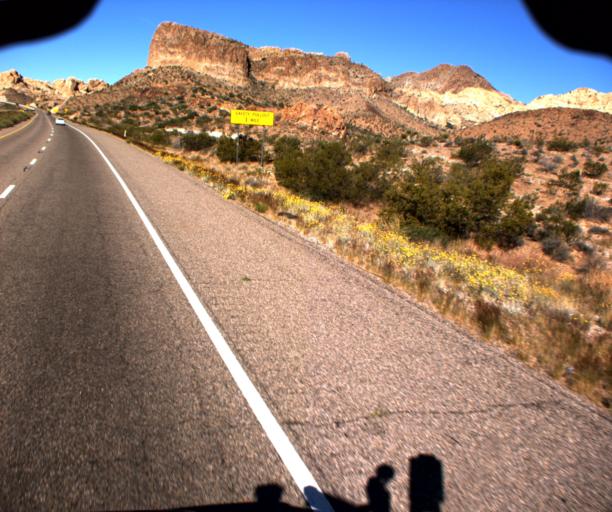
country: US
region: Arizona
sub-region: Mohave County
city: Golden Valley
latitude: 35.2278
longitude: -114.3763
